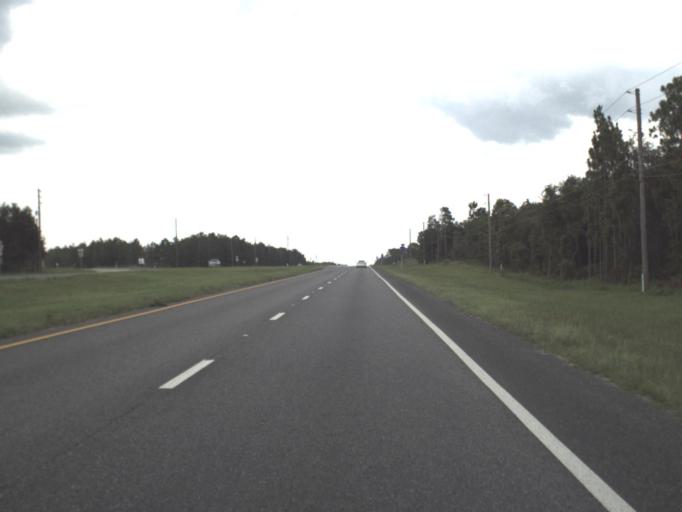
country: US
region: Florida
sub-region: Levy County
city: East Bronson
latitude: 29.4216
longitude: -82.5770
